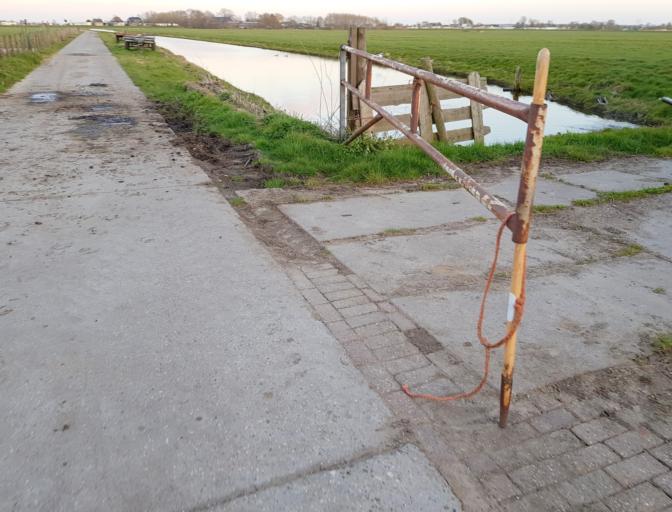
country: NL
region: South Holland
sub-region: Gemeente Teylingen
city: Sassenheim
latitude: 52.1958
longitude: 4.5374
